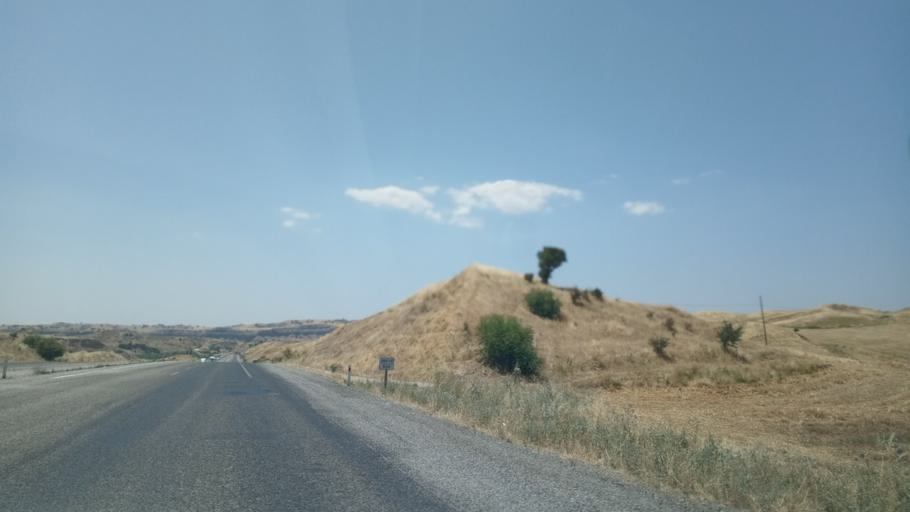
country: TR
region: Batman
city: Kozluk
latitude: 38.1608
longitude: 41.4184
